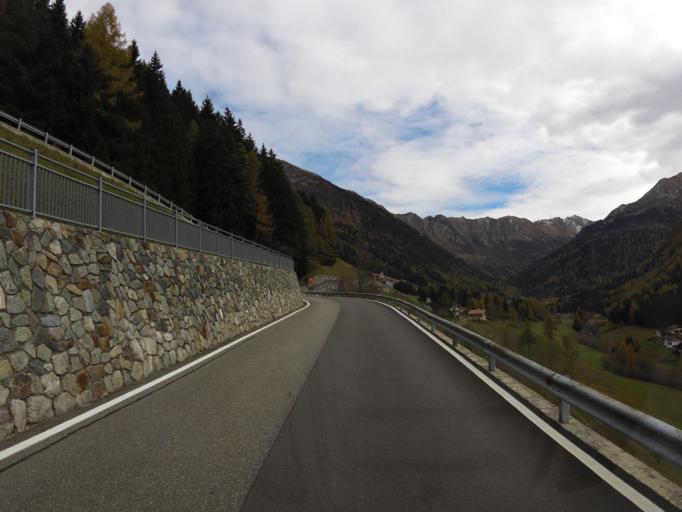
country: IT
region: Trentino-Alto Adige
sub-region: Bolzano
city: Racines
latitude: 46.8270
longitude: 11.2943
